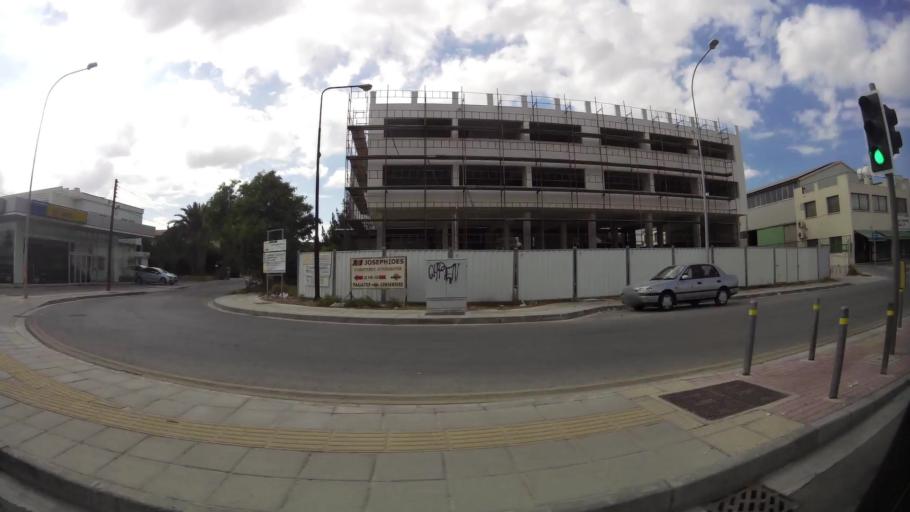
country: CY
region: Lefkosia
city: Nicosia
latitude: 35.1811
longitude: 33.3947
